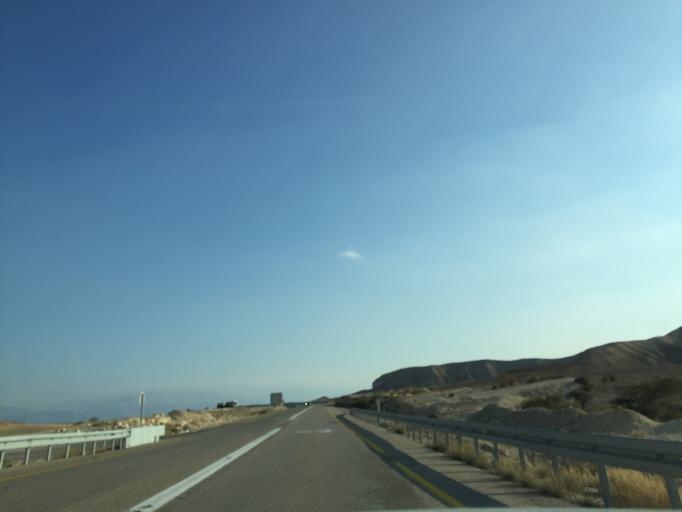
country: IL
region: Southern District
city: `En Boqeq
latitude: 31.1704
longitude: 35.3157
